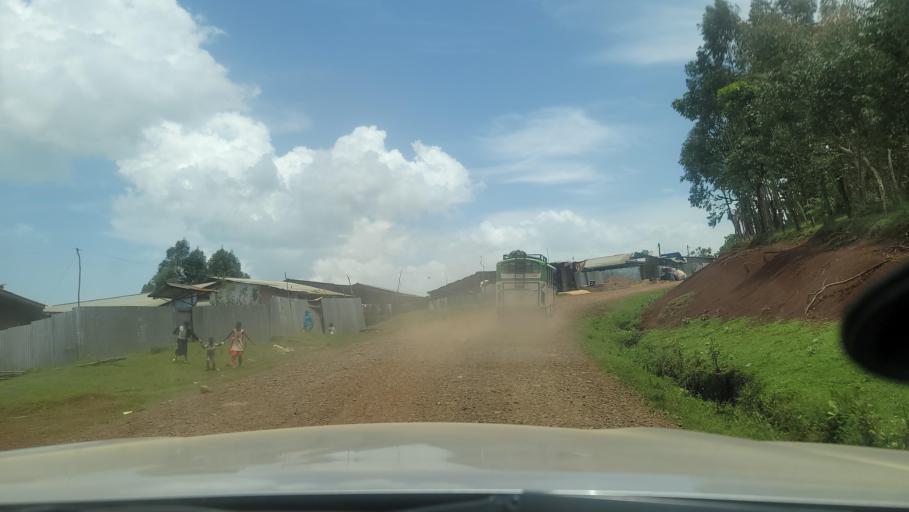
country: ET
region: Oromiya
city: Agaro
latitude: 7.7380
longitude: 36.2557
